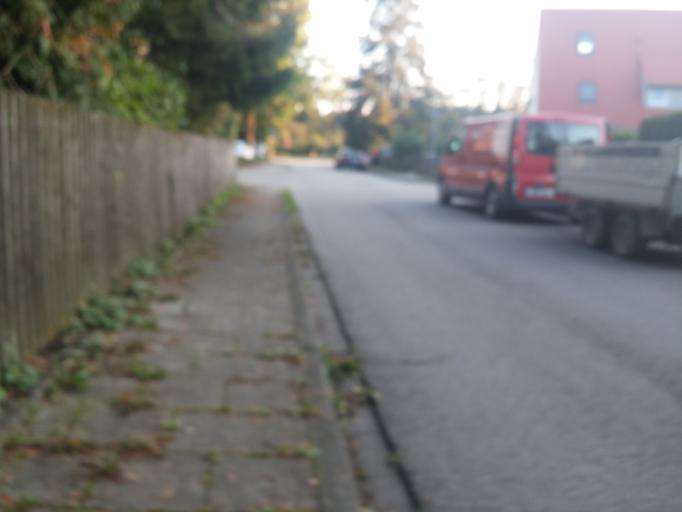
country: DE
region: Bavaria
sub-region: Upper Bavaria
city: Vaterstetten
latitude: 48.1044
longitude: 11.7486
